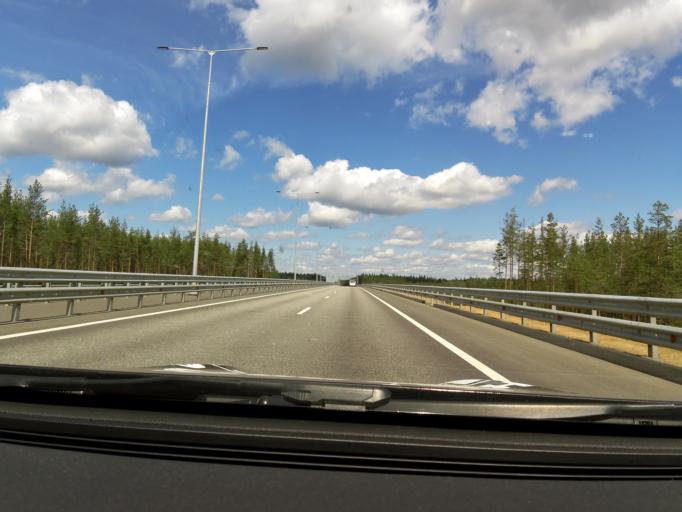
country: RU
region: Tverskaya
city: Krasnomayskiy
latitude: 57.6058
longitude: 34.2492
